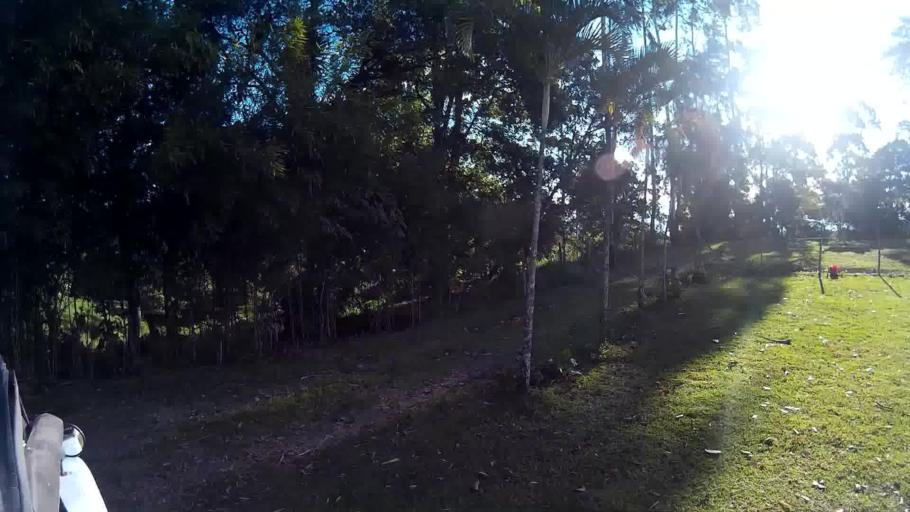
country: CO
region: Quindio
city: Filandia
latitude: 4.7137
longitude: -75.6492
